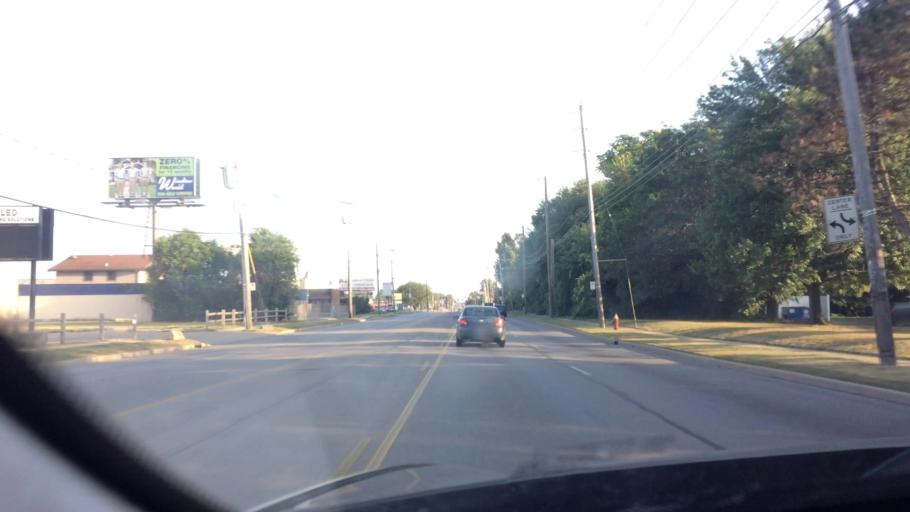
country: US
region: Ohio
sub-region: Lucas County
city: Ottawa Hills
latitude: 41.6428
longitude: -83.6260
